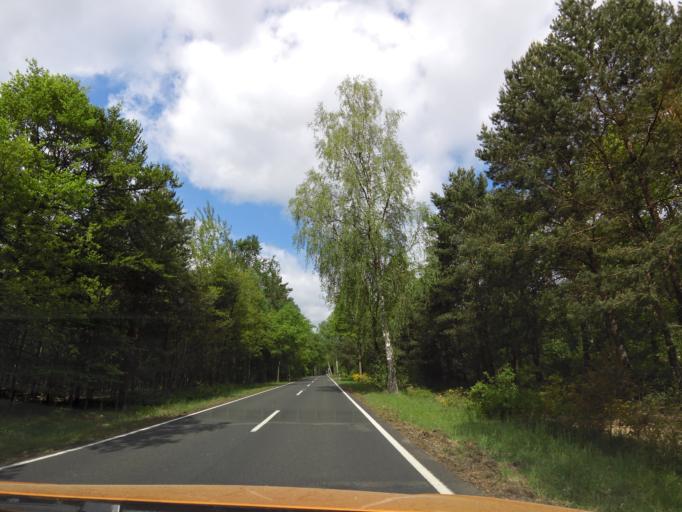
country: DE
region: Brandenburg
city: Gorzke
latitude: 52.0741
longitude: 12.2831
